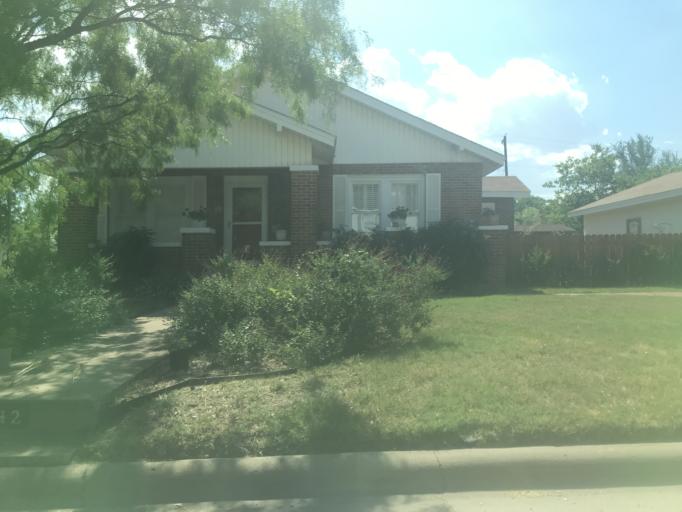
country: US
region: Texas
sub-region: Taylor County
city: Abilene
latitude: 32.4347
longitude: -99.7492
